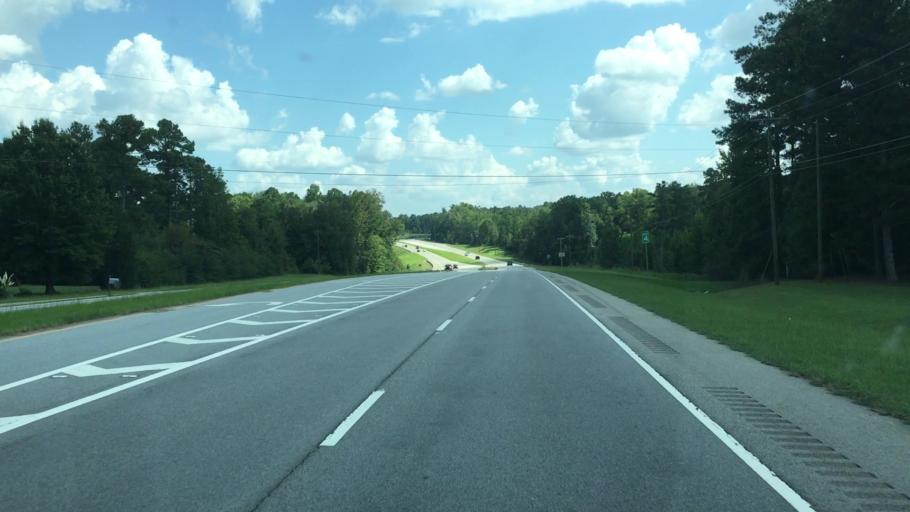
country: US
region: Georgia
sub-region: Putnam County
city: Eatonton
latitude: 33.2442
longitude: -83.3239
